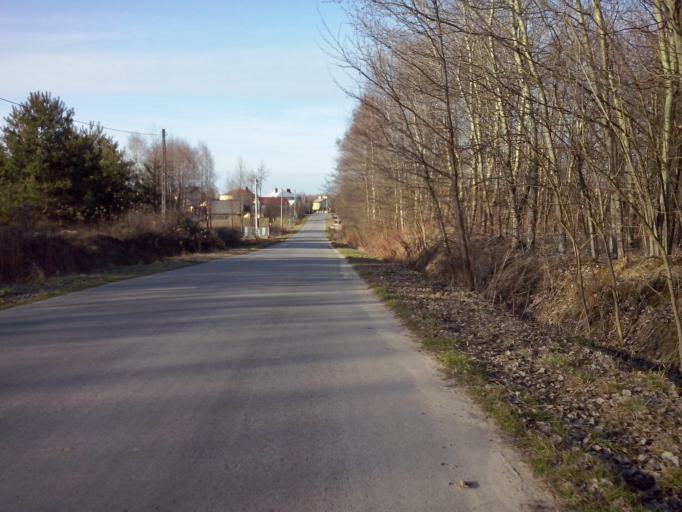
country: PL
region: Subcarpathian Voivodeship
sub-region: Powiat nizanski
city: Krzeszow
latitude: 50.4131
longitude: 22.3505
